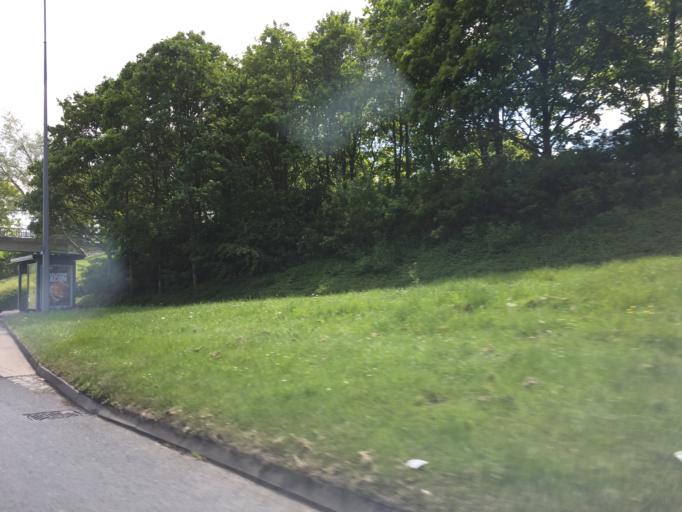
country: GB
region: England
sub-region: Milton Keynes
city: Milton Keynes
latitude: 52.0323
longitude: -0.7470
